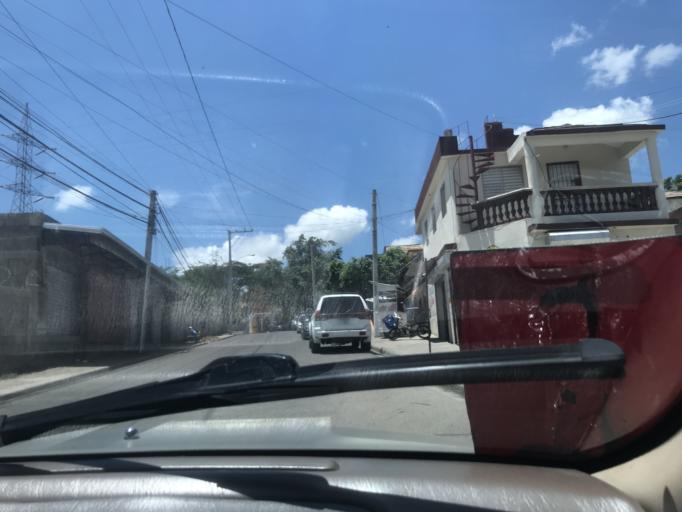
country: DO
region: Santiago
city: Santiago de los Caballeros
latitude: 19.4164
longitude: -70.6869
